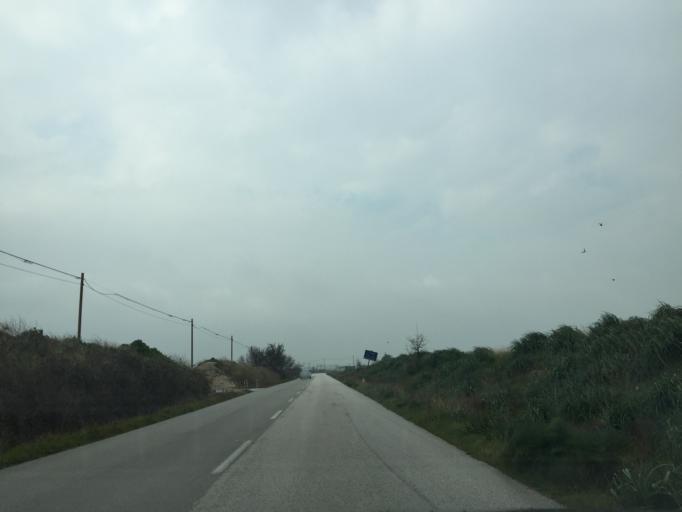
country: IT
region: Apulia
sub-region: Provincia di Foggia
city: Castelluccio dei Sauri
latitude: 41.3975
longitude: 15.4231
